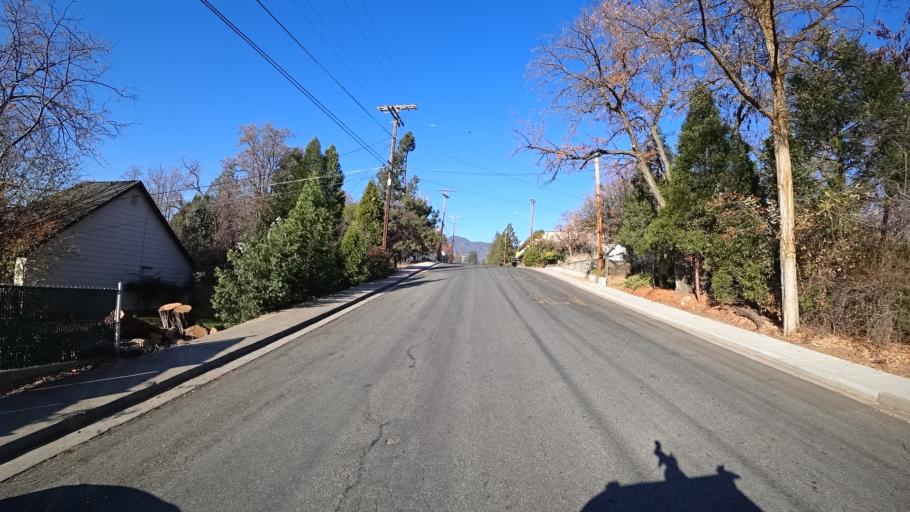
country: US
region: California
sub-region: Siskiyou County
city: Yreka
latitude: 41.7368
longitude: -122.6377
